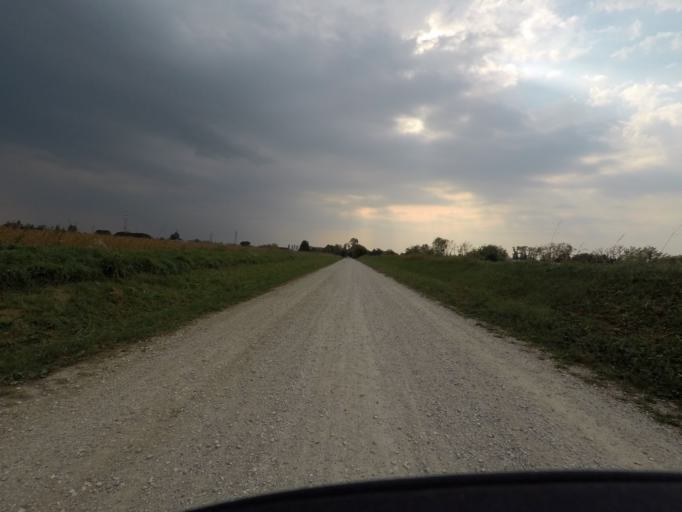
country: IT
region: Friuli Venezia Giulia
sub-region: Provincia di Udine
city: Tavagnacco
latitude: 46.1060
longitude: 13.2401
